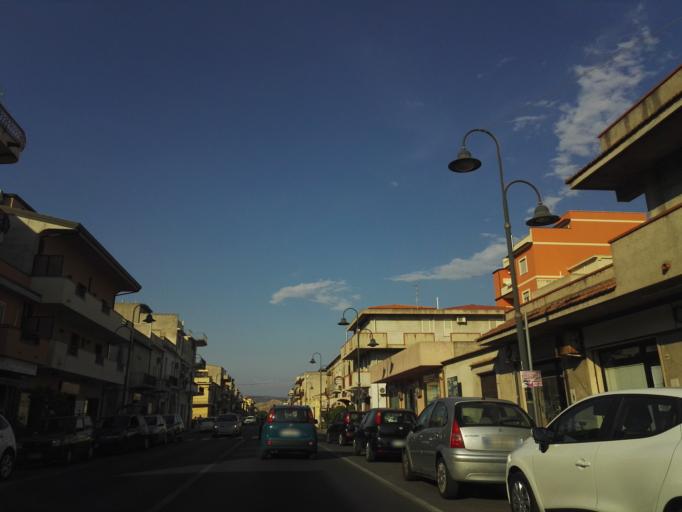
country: IT
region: Calabria
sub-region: Provincia di Reggio Calabria
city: Marina di Gioiosa Ionica
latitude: 38.3002
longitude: 16.3295
